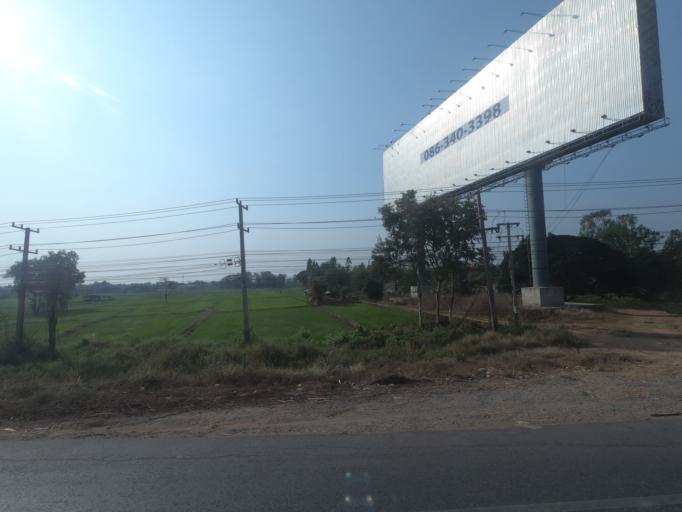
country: TH
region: Khon Kaen
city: Khon Kaen
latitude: 16.3683
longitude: 102.8076
